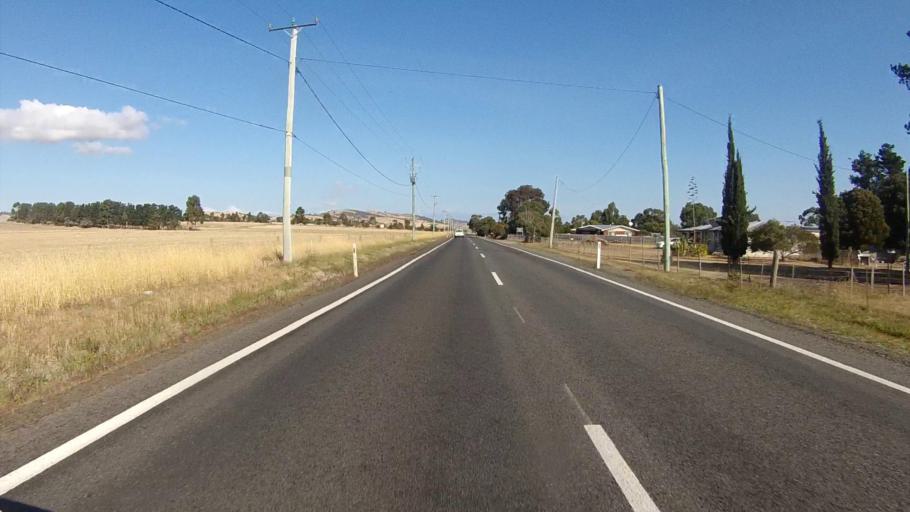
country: AU
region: Tasmania
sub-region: Sorell
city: Sorell
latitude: -42.7317
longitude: 147.5276
